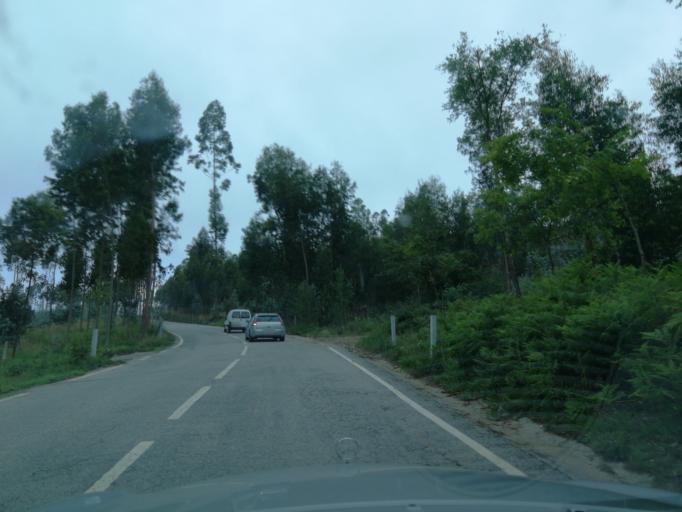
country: PT
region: Braga
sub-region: Braga
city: Braga
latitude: 41.5254
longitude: -8.3827
